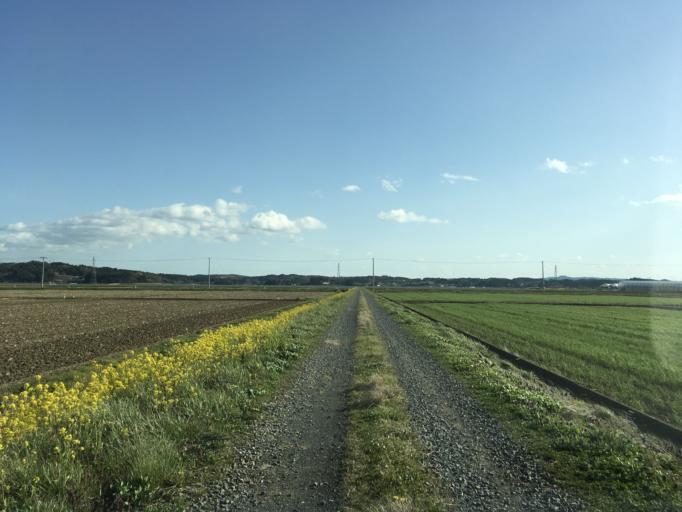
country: JP
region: Miyagi
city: Wakuya
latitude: 38.6622
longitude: 141.2418
